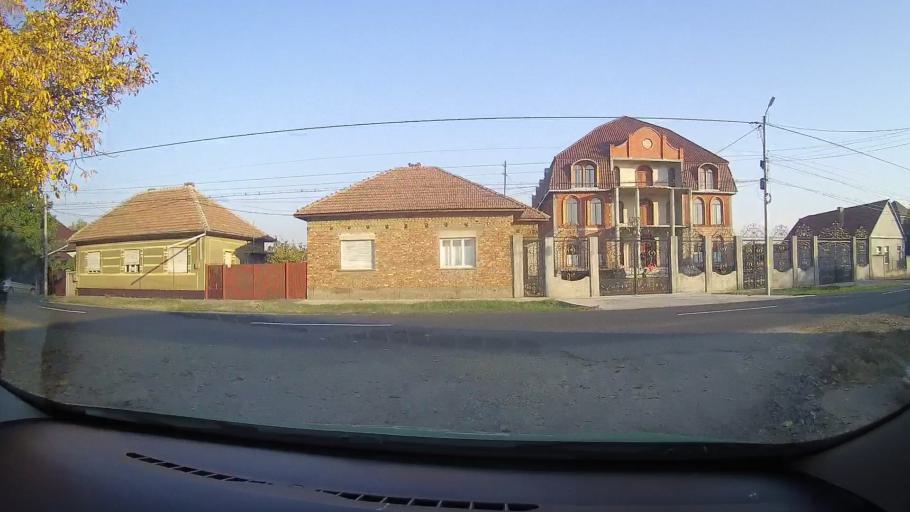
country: RO
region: Arad
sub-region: Comuna Curtici
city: Curtici
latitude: 46.3436
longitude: 21.3116
